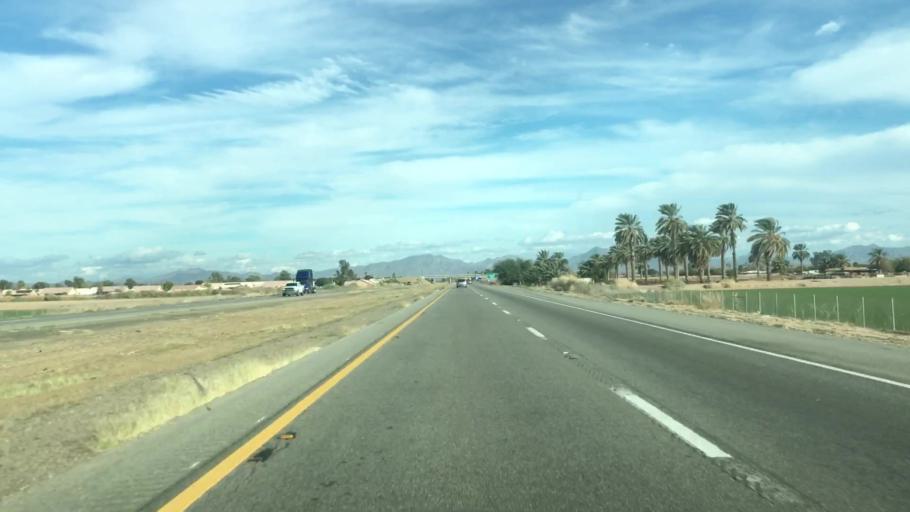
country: US
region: California
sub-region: Riverside County
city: Blythe
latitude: 33.6065
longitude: -114.6335
